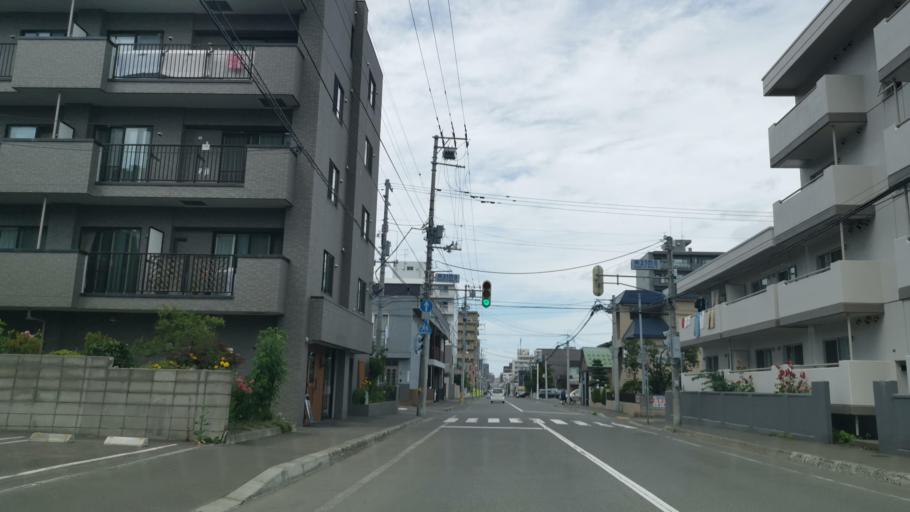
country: JP
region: Hokkaido
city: Sapporo
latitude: 43.0320
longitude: 141.3482
